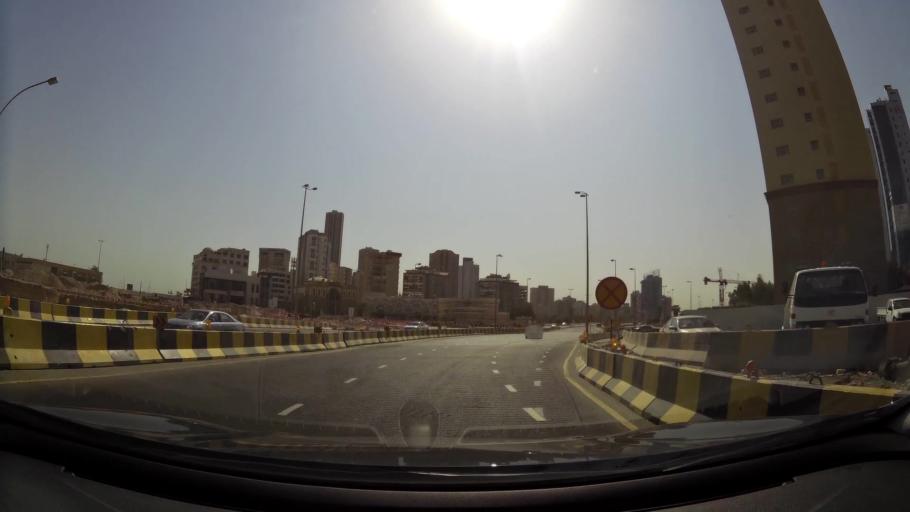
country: KW
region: Al Asimah
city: Ad Dasmah
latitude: 29.3805
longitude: 47.9964
